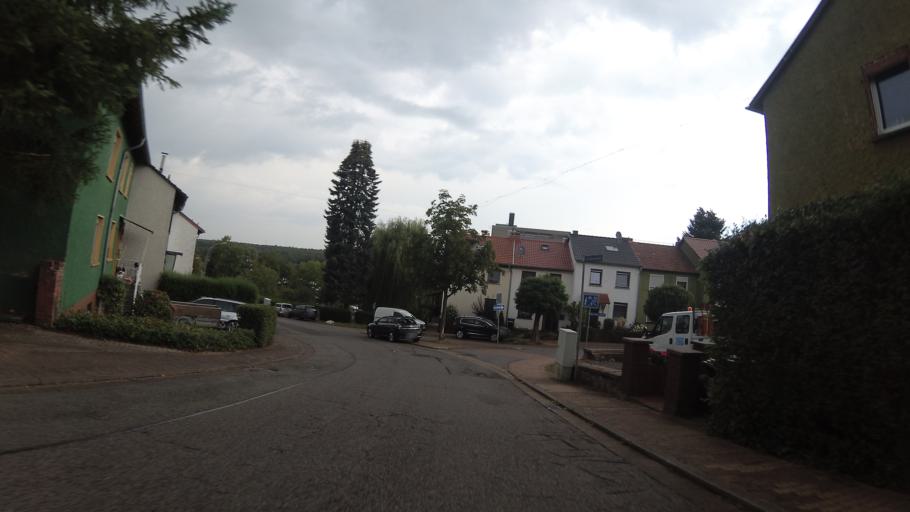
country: DE
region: Saarland
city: Sulzbach
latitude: 49.2874
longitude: 7.0723
